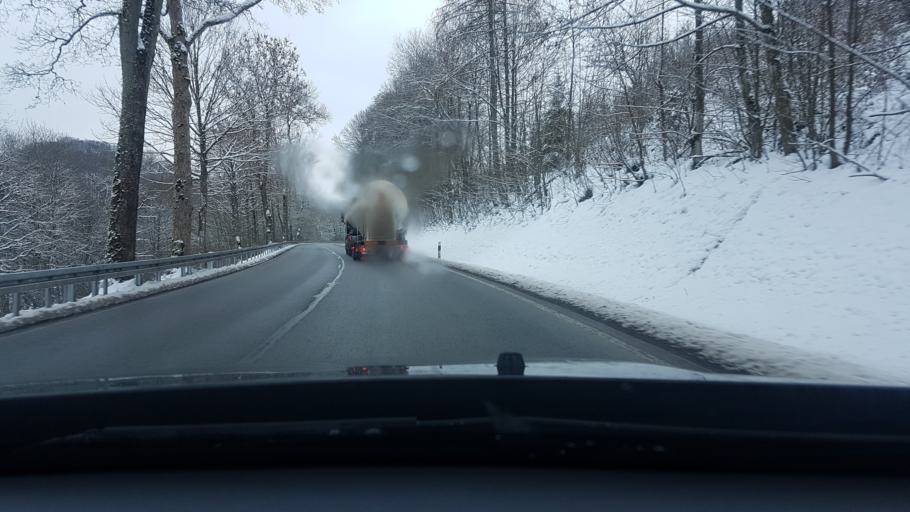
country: DE
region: North Rhine-Westphalia
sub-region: Regierungsbezirk Arnsberg
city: Medebach
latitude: 51.2954
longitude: 8.7209
